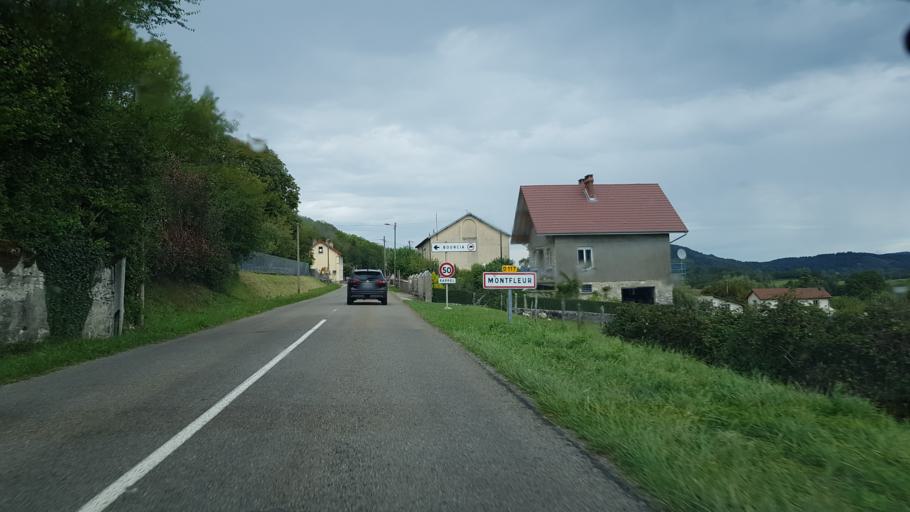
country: FR
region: Rhone-Alpes
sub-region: Departement de l'Ain
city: Cuisiat
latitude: 46.3280
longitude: 5.4379
